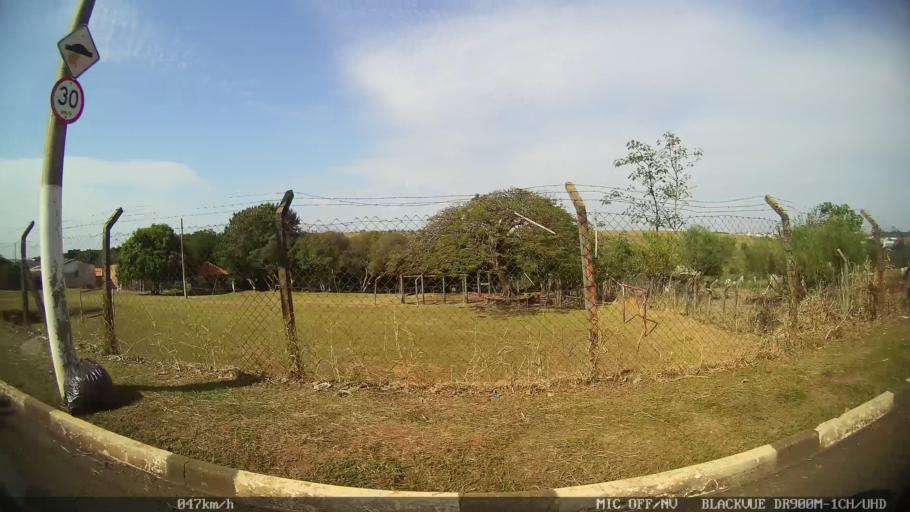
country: BR
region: Sao Paulo
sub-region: Paulinia
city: Paulinia
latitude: -22.7915
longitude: -47.1825
